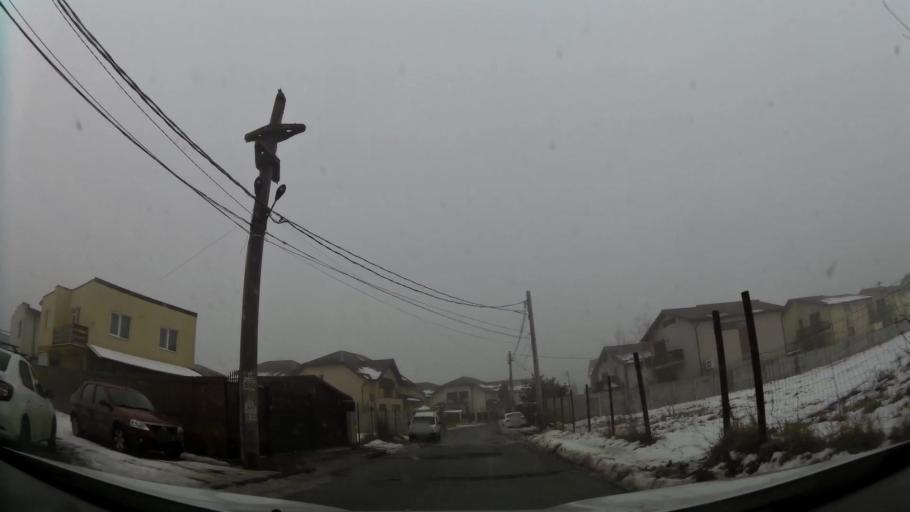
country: RO
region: Ilfov
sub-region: Comuna Chiajna
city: Chiajna
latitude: 44.4561
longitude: 25.9732
